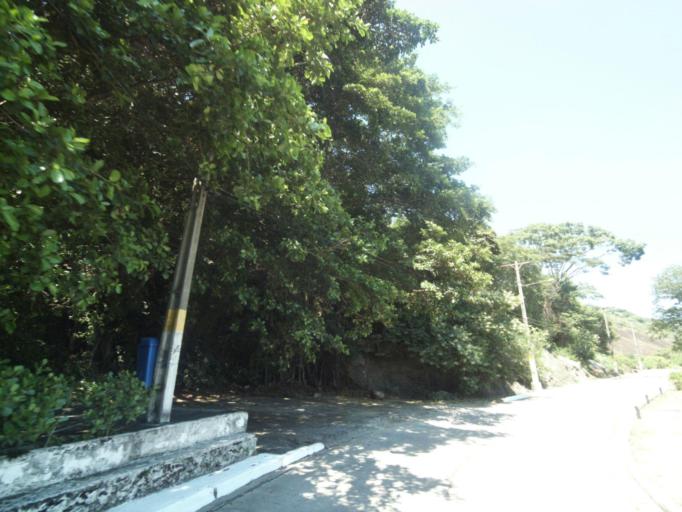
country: BR
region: Rio de Janeiro
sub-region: Niteroi
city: Niteroi
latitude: -22.9342
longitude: -43.1256
